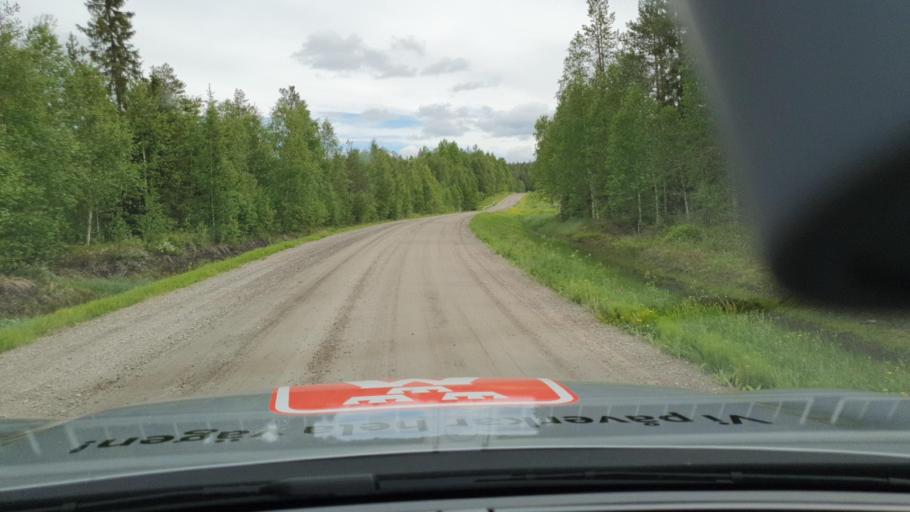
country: SE
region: Norrbotten
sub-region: Kalix Kommun
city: Kalix
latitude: 65.9413
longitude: 23.5332
